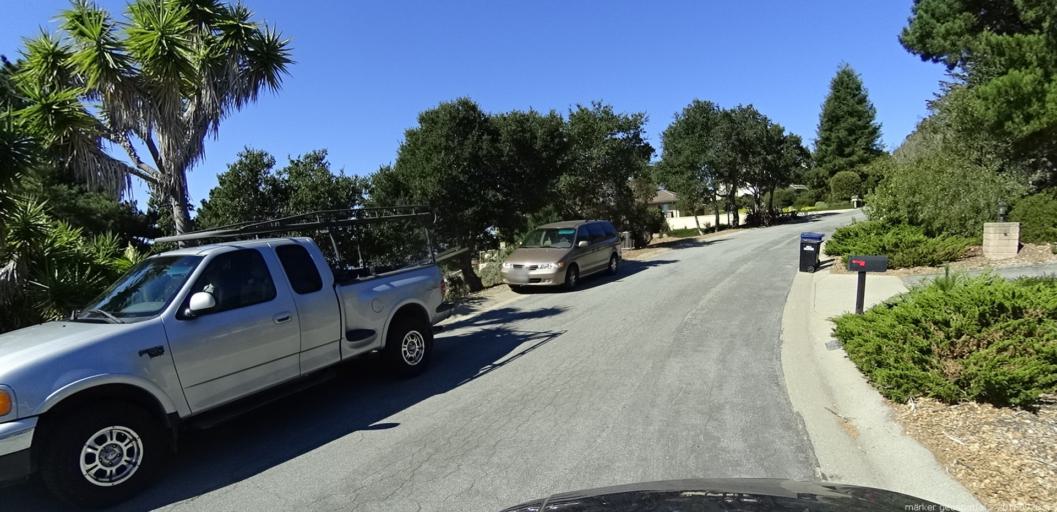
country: US
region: California
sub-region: Monterey County
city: Carmel-by-the-Sea
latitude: 36.5612
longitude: -121.8971
